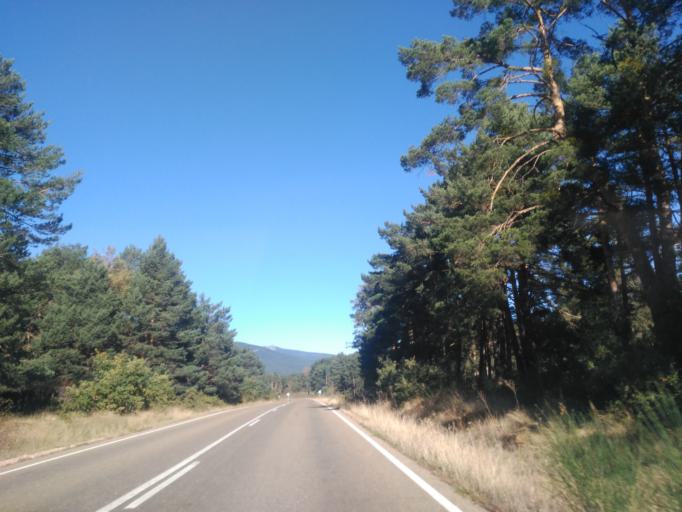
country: ES
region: Castille and Leon
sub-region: Provincia de Soria
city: Vinuesa
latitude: 41.9178
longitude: -2.7562
